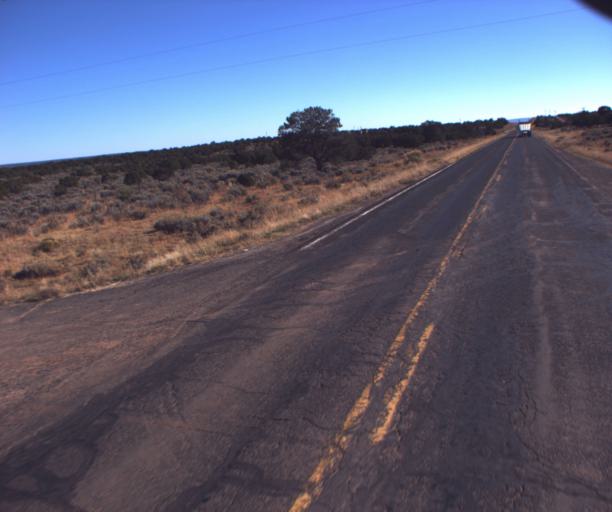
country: US
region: Arizona
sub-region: Apache County
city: Ganado
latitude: 35.5789
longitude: -109.5360
